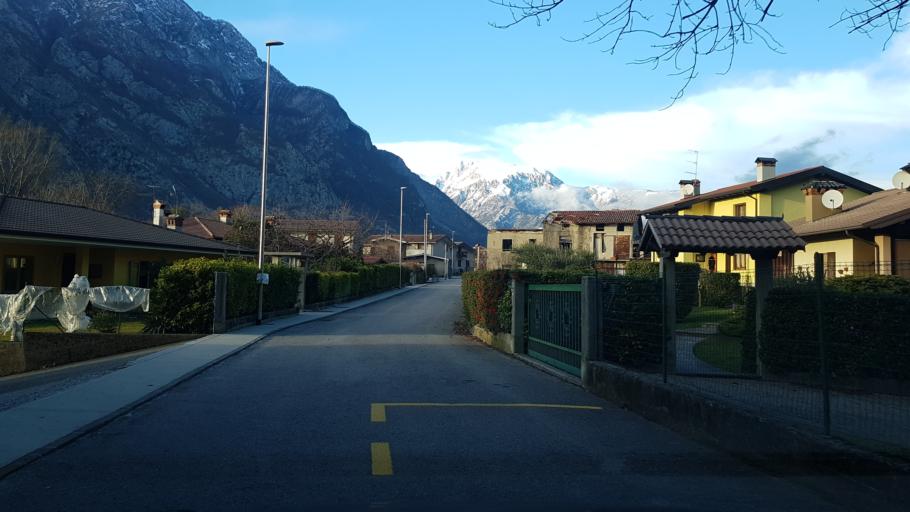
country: IT
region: Friuli Venezia Giulia
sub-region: Provincia di Udine
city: Venzone
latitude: 46.3259
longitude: 13.1410
